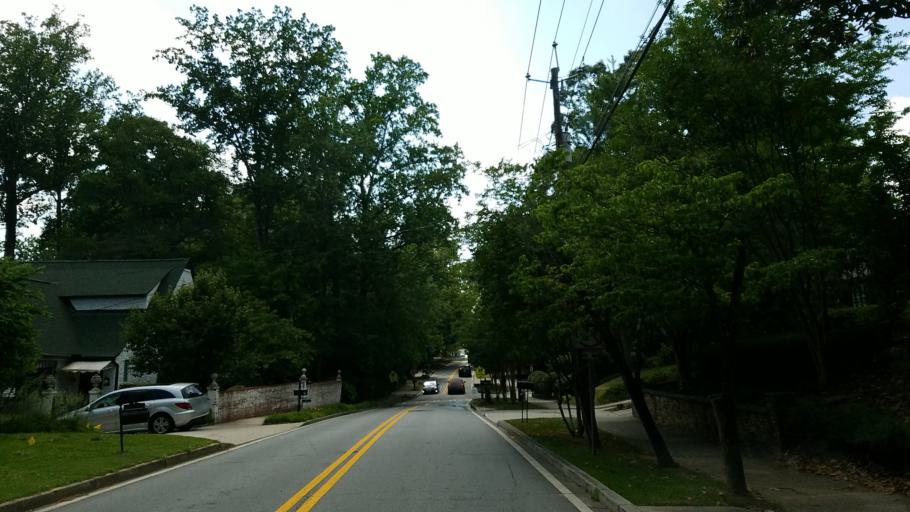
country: US
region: Georgia
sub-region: DeKalb County
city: North Atlanta
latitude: 33.8287
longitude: -84.3828
